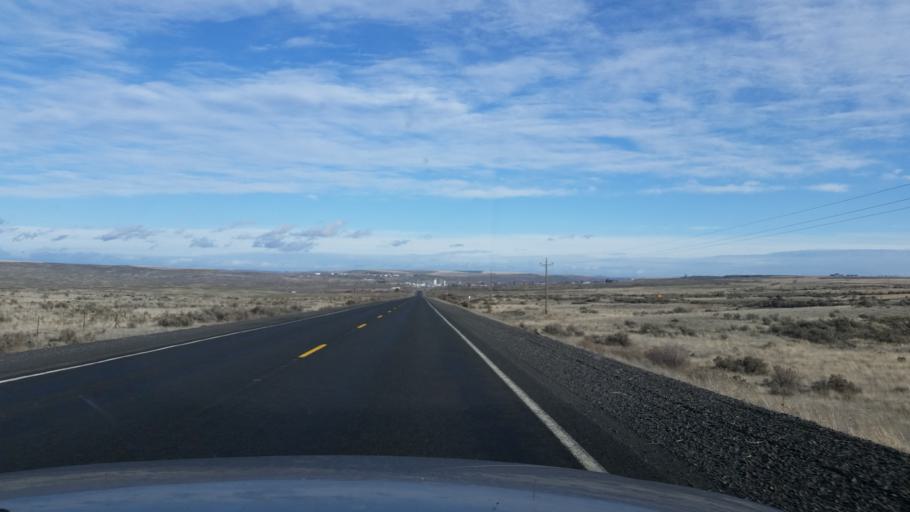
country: US
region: Washington
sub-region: Adams County
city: Ritzville
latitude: 47.3187
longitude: -118.7387
